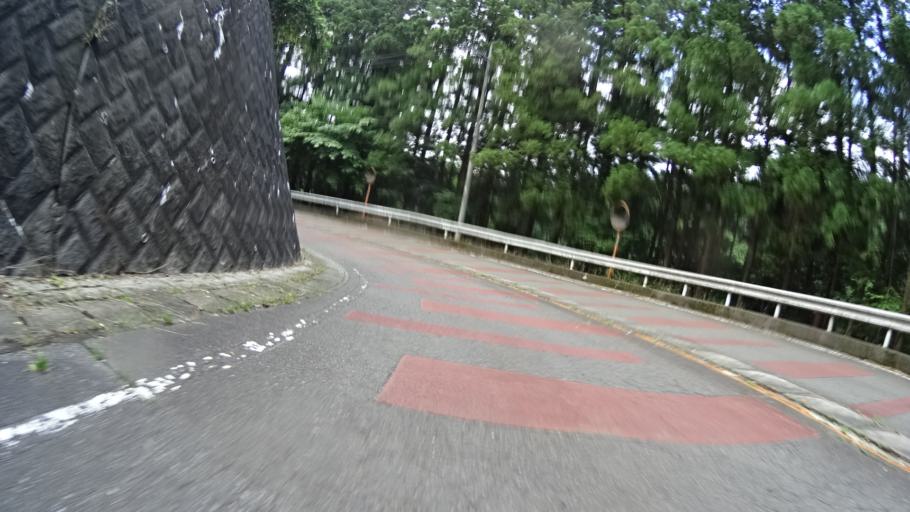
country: JP
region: Kanagawa
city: Hadano
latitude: 35.4998
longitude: 139.2319
